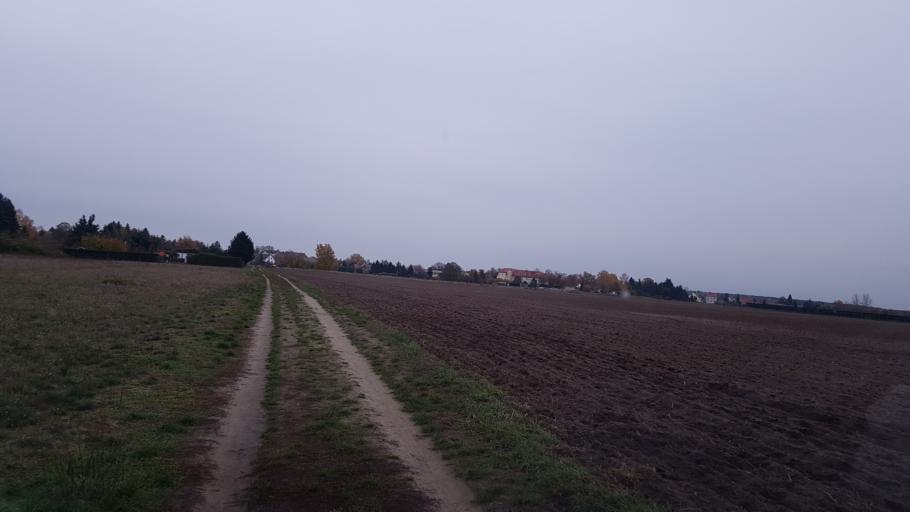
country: DE
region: Brandenburg
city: Finsterwalde
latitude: 51.6170
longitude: 13.7057
